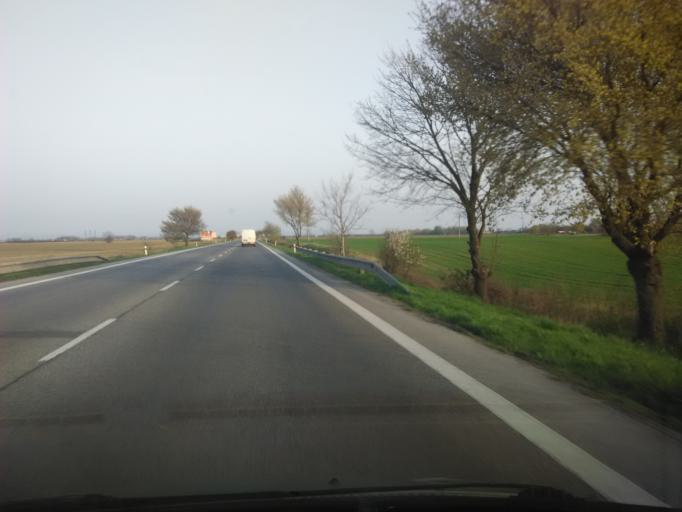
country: SK
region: Nitriansky
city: Sellye
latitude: 48.1683
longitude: 17.8353
